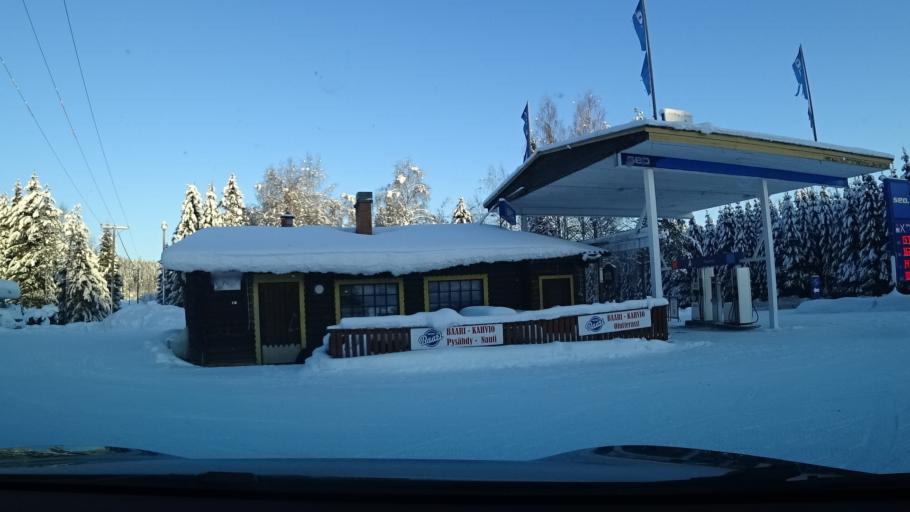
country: FI
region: Southern Savonia
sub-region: Savonlinna
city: Heinaevesi
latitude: 62.5246
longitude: 28.4655
